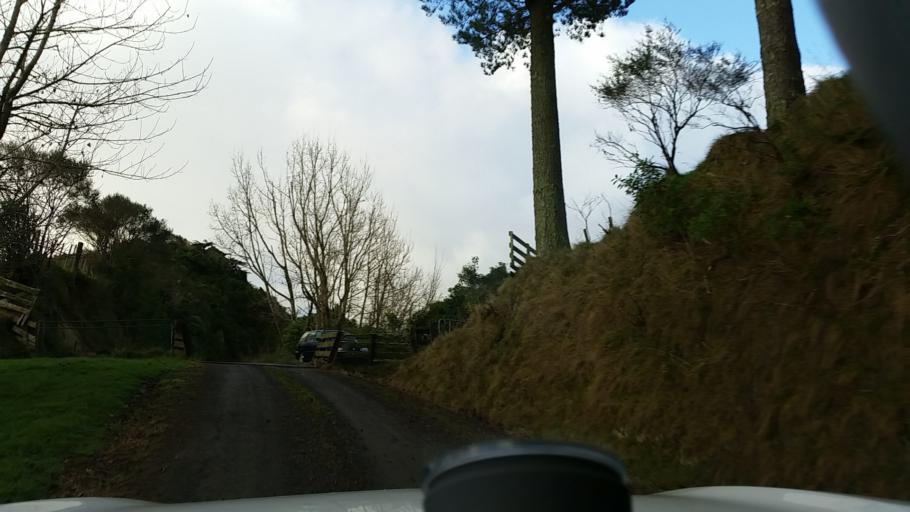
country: NZ
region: Taranaki
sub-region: South Taranaki District
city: Eltham
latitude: -39.4378
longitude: 174.4488
